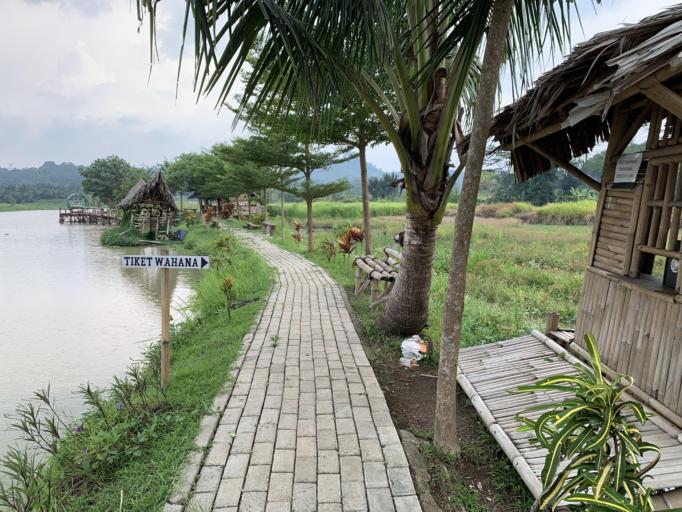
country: ID
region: West Java
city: Serpong
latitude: -6.3653
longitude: 106.5831
